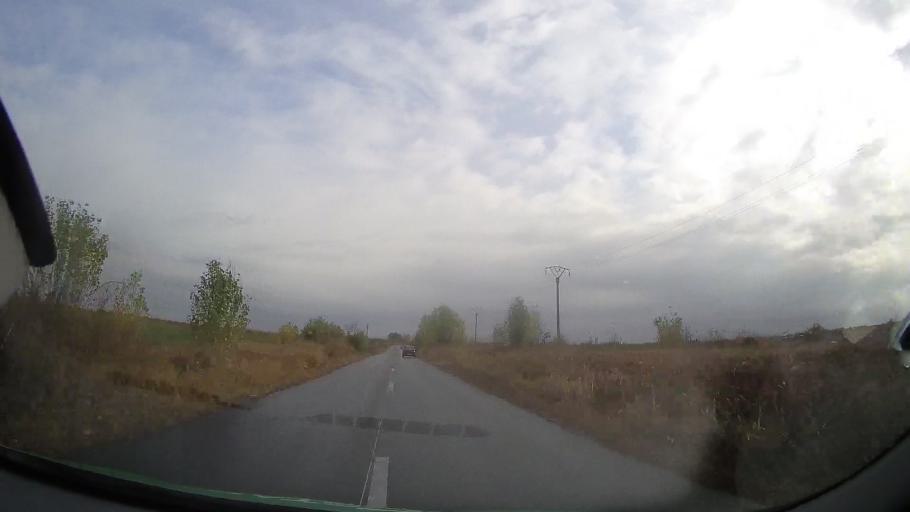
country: RO
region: Ialomita
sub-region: Comuna Maia
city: Maia
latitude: 44.7491
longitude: 26.3930
